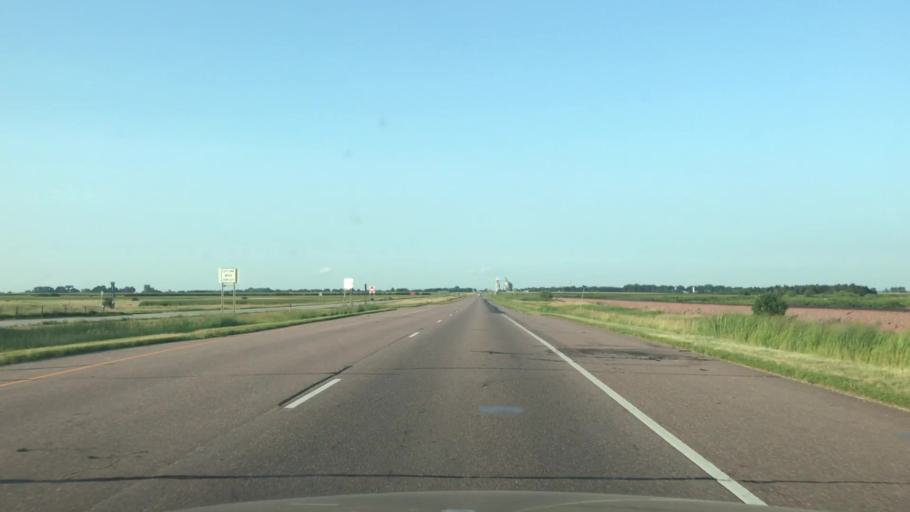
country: US
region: Minnesota
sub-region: Jackson County
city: Lakefield
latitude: 43.7767
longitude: -95.3510
